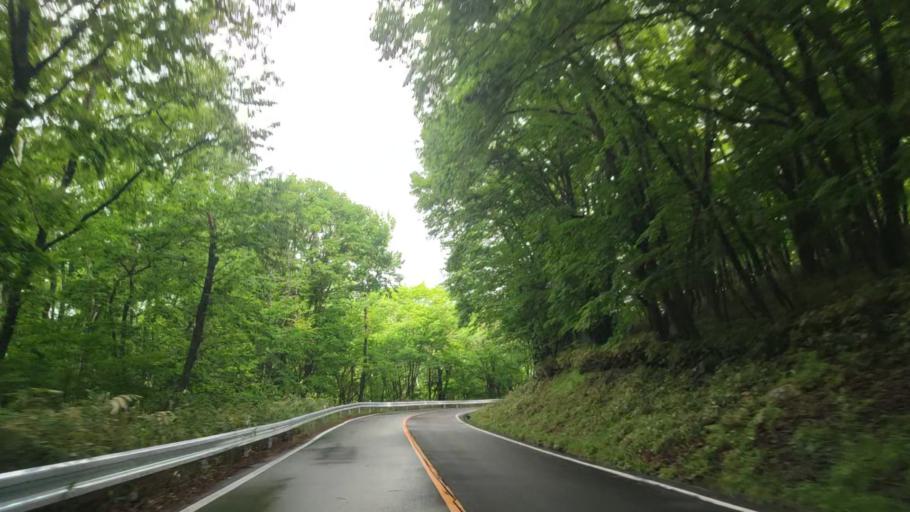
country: JP
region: Nagano
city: Chino
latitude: 36.0729
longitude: 138.2894
